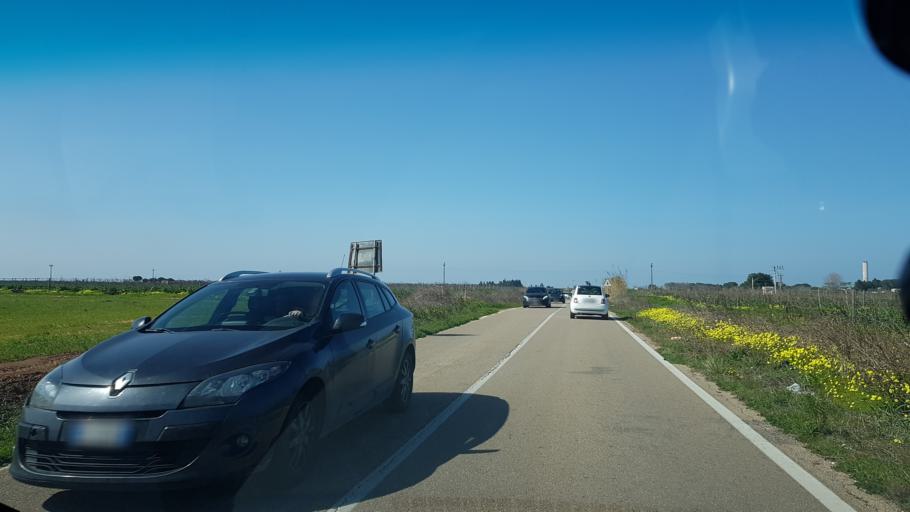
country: IT
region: Apulia
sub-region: Provincia di Brindisi
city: Torchiarolo
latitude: 40.5319
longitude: 18.0653
